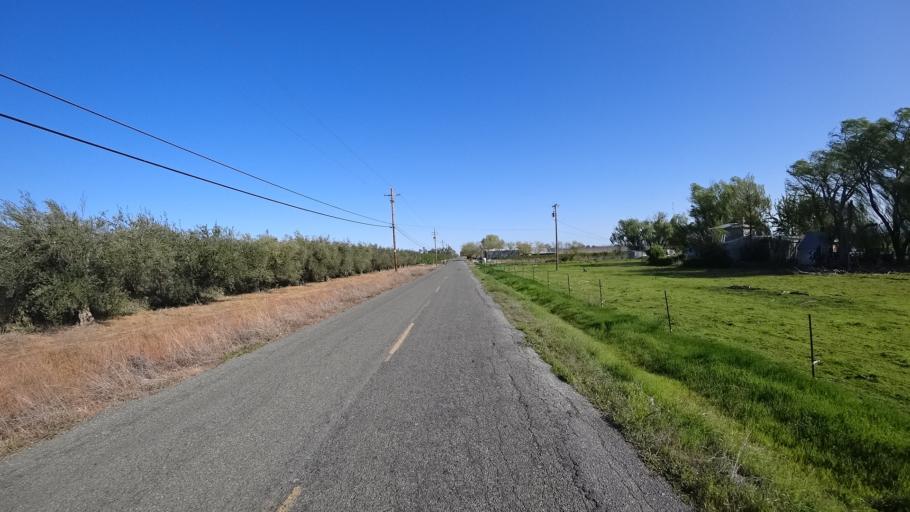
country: US
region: California
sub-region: Glenn County
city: Orland
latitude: 39.7996
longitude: -122.1040
